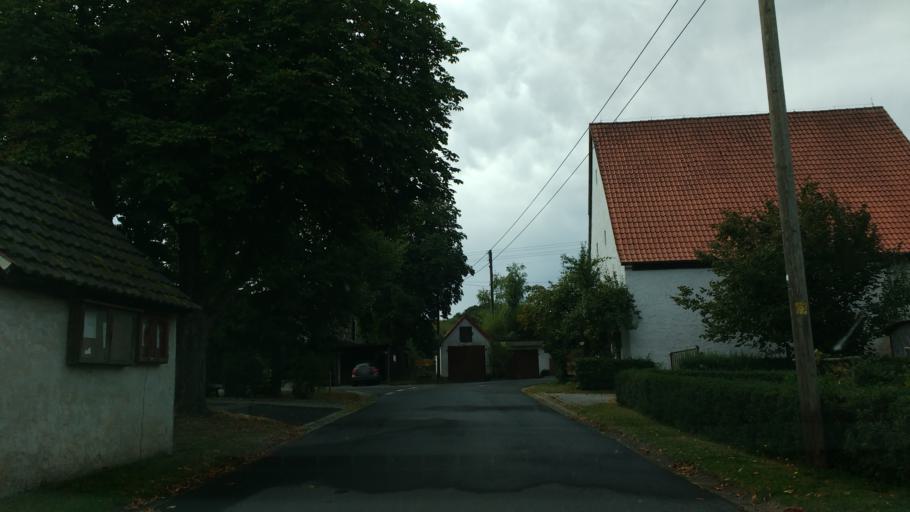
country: DE
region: Bavaria
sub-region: Regierungsbezirk Unterfranken
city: Geiselwind
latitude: 49.7822
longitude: 10.5234
